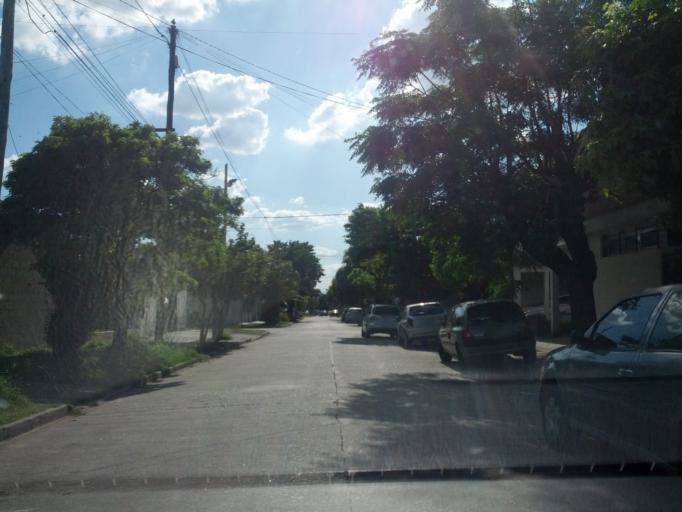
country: AR
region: Buenos Aires
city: San Justo
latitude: -34.6486
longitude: -58.5813
